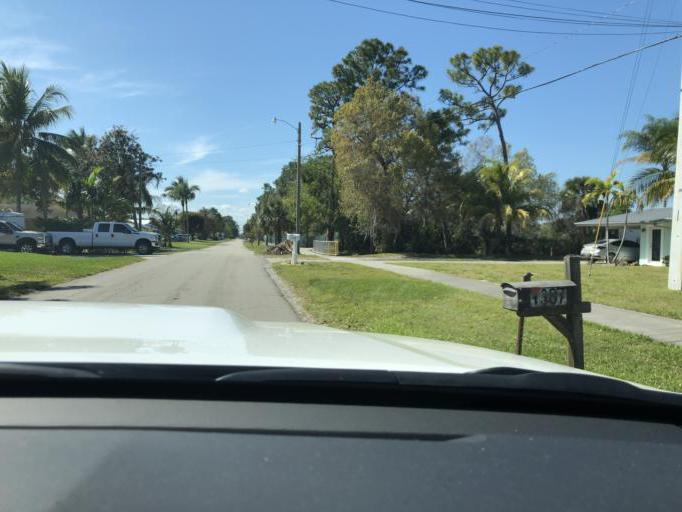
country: US
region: Florida
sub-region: Martin County
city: Palm City
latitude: 27.1684
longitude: -80.2709
